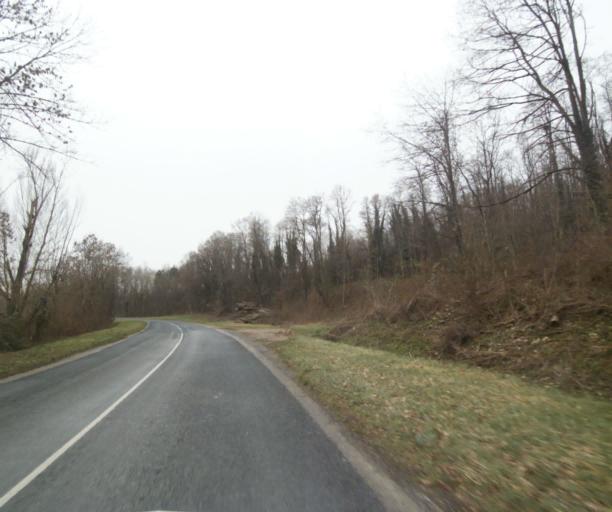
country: FR
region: Champagne-Ardenne
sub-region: Departement de la Haute-Marne
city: Bienville
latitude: 48.5708
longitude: 5.0374
